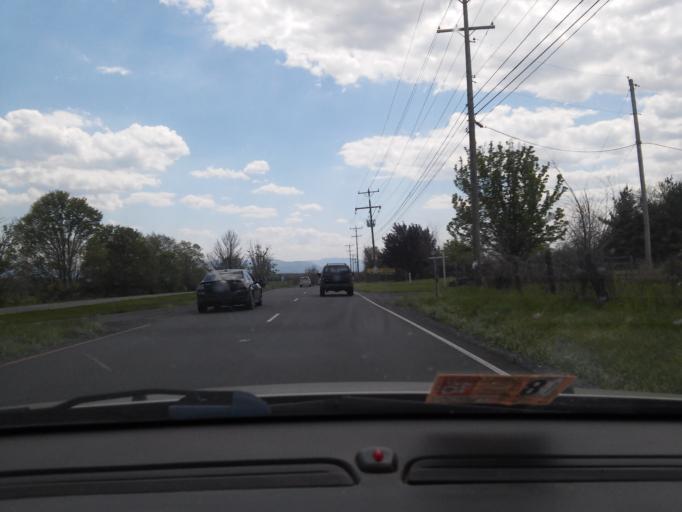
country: US
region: Virginia
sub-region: Frederick County
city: Stephens City
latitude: 39.0475
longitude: -78.1449
